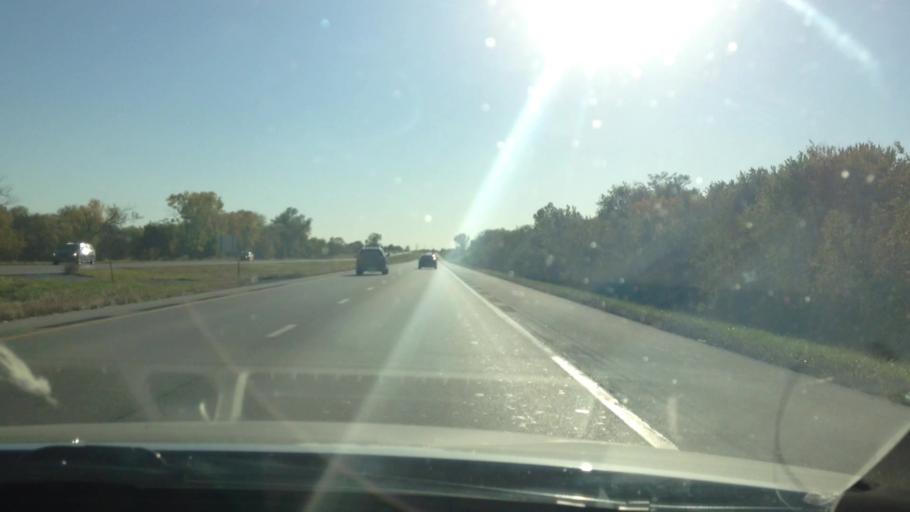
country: US
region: Kansas
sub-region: Johnson County
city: Gardner
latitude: 38.7782
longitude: -94.9327
